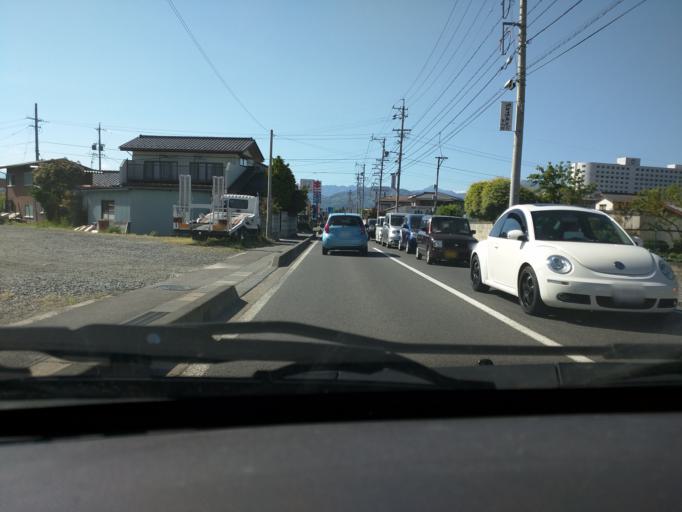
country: JP
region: Nagano
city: Nagano-shi
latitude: 36.5675
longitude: 138.2013
